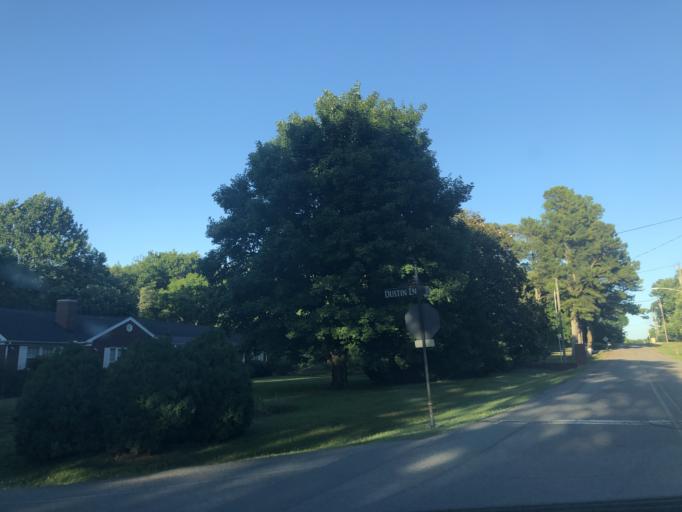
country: US
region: Tennessee
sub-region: Davidson County
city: Oak Hill
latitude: 36.0818
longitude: -86.7855
